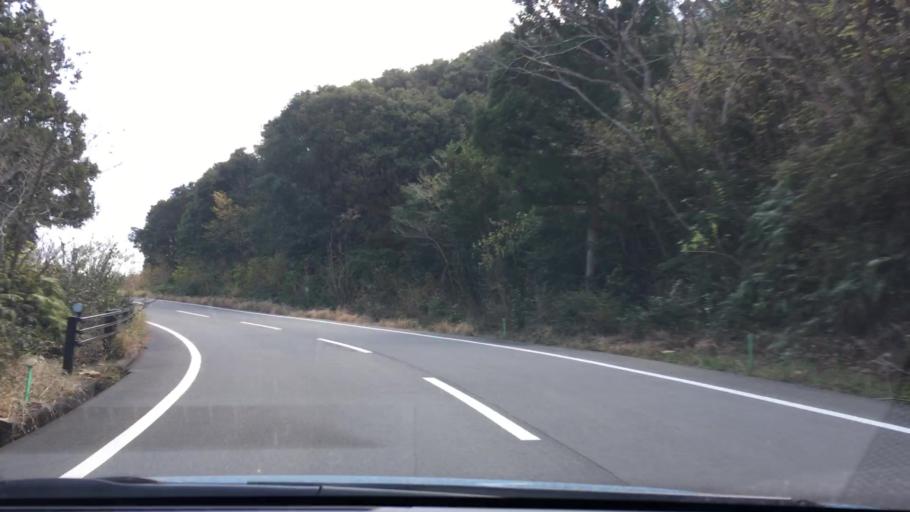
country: JP
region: Mie
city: Toba
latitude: 34.4313
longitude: 136.9130
